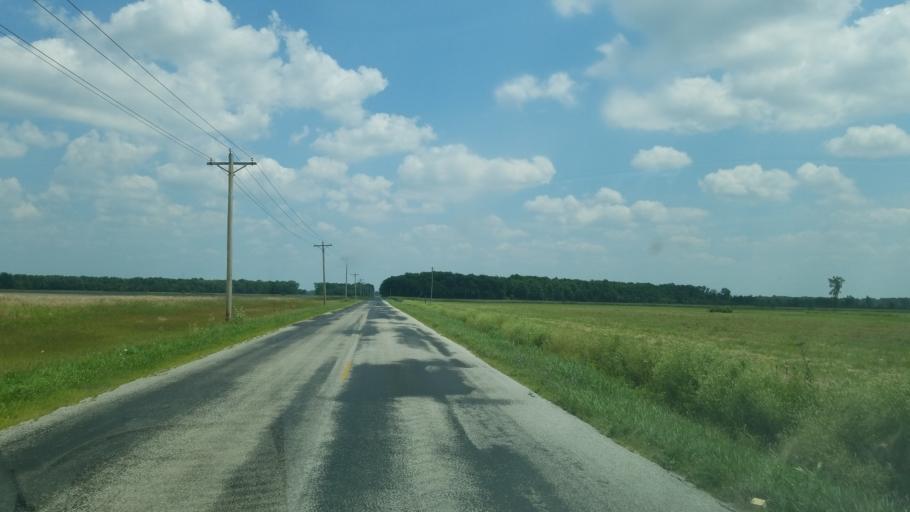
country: US
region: Ohio
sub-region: Wood County
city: North Baltimore
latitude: 41.2410
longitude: -83.6968
